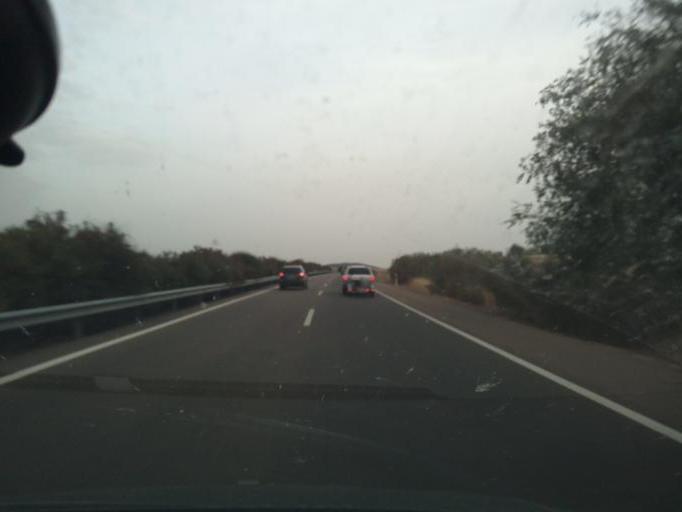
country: ES
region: Extremadura
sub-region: Provincia de Badajoz
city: Merida
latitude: 38.9448
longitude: -6.3062
